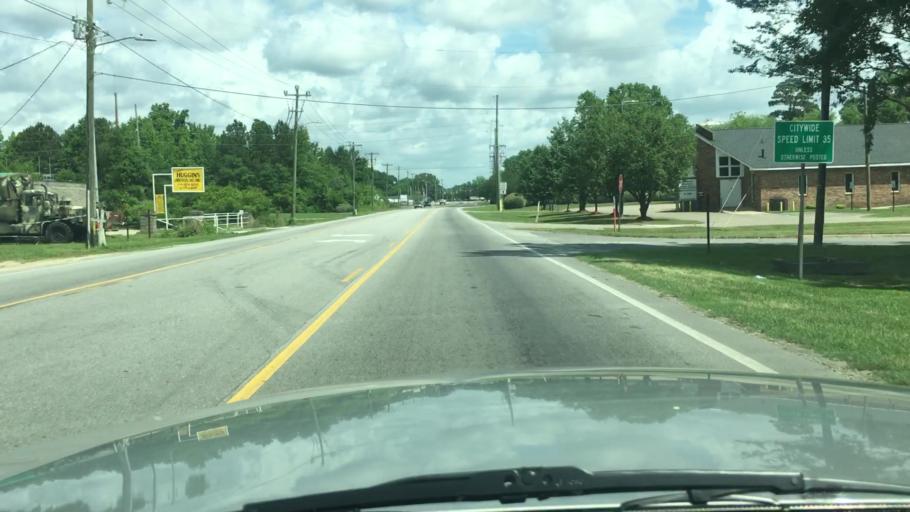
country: US
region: North Carolina
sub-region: Cumberland County
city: Fayetteville
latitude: 35.0306
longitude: -78.8721
